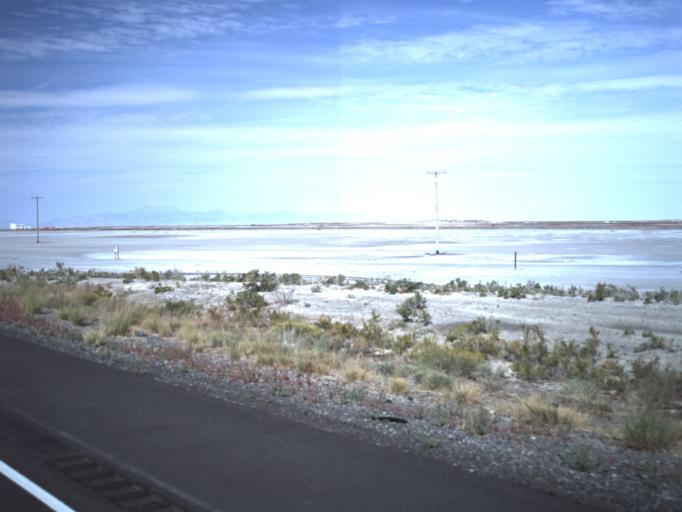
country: US
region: Utah
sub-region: Tooele County
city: Wendover
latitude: 40.7276
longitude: -113.2799
